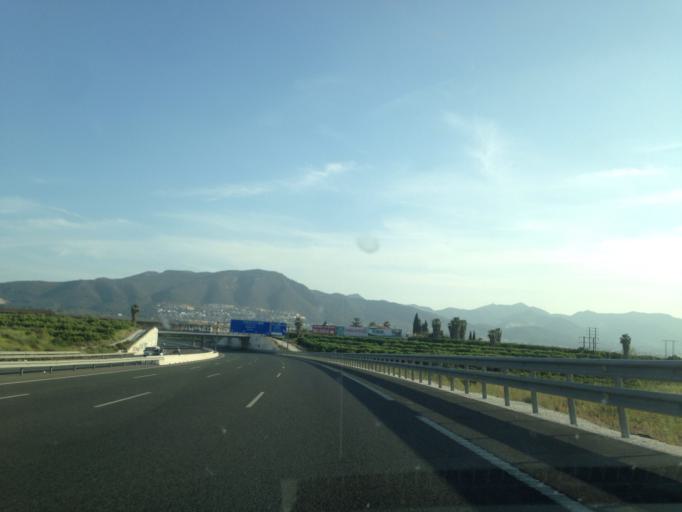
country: ES
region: Andalusia
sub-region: Provincia de Malaga
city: Alhaurin de la Torre
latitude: 36.6903
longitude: -4.5264
